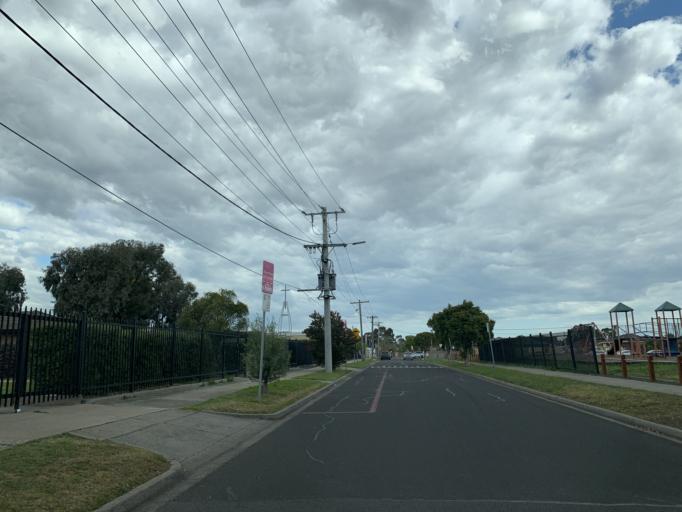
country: AU
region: Victoria
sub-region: Moonee Valley
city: Keilor East
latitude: -37.7438
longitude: 144.8587
